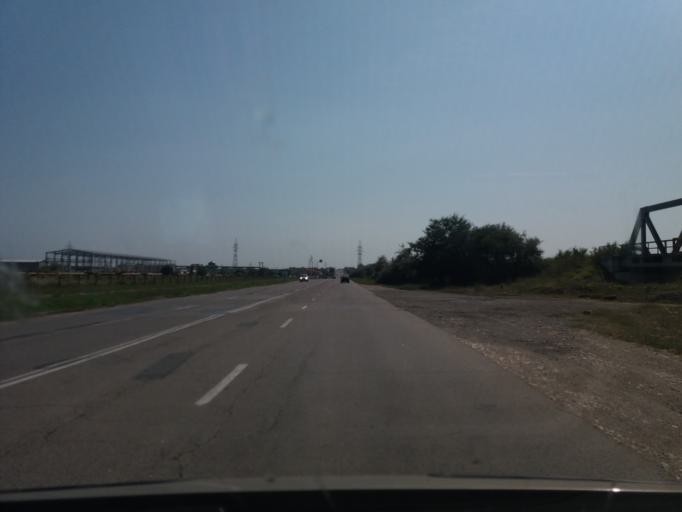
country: RO
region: Constanta
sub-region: Comuna Navodari
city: Navodari
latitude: 44.3317
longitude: 28.6304
